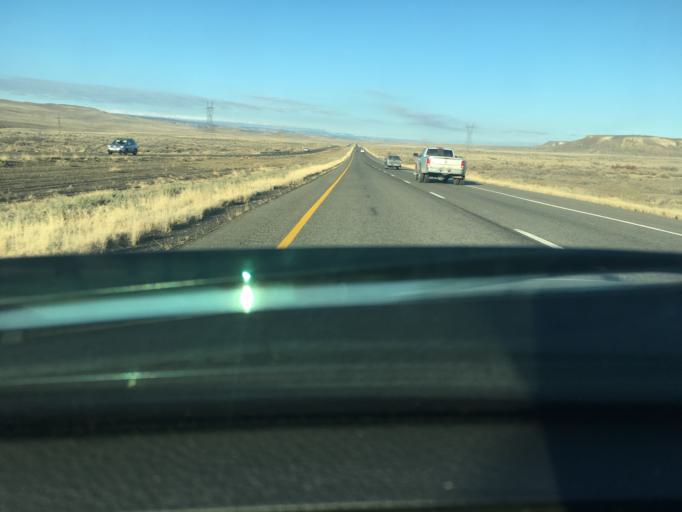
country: US
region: Colorado
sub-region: Delta County
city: Delta
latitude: 38.7586
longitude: -108.1866
